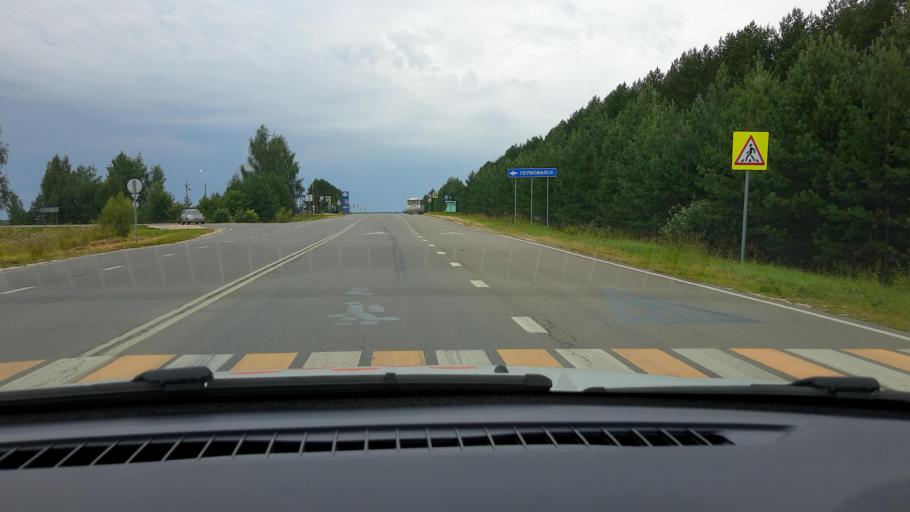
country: RU
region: Nizjnij Novgorod
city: Vyyezdnoye
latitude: 55.1515
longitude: 43.5703
